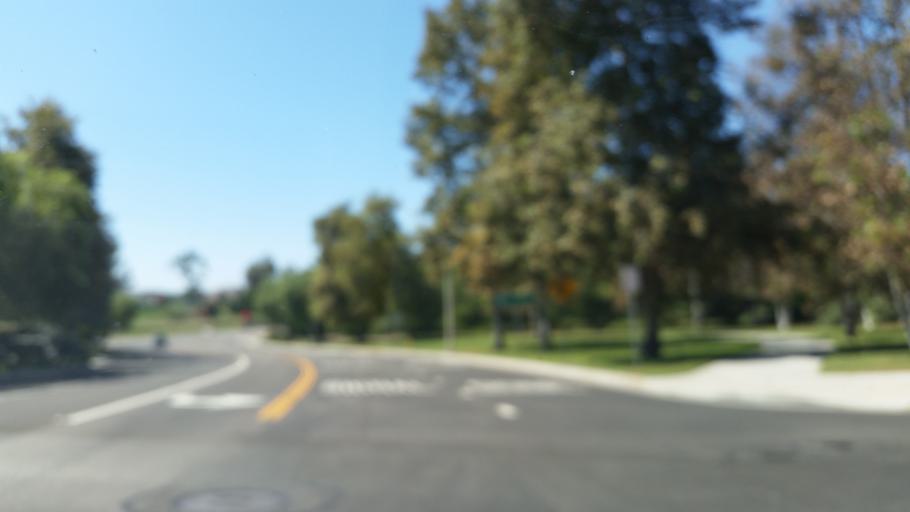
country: US
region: California
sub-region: Orange County
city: San Clemente
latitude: 33.4620
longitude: -117.5912
